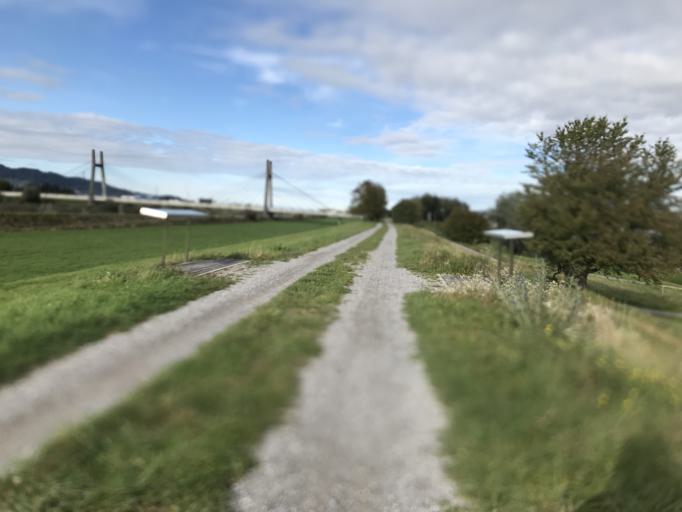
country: CH
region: Saint Gallen
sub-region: Wahlkreis Rheintal
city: Diepoldsau
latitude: 47.3875
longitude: 9.6465
